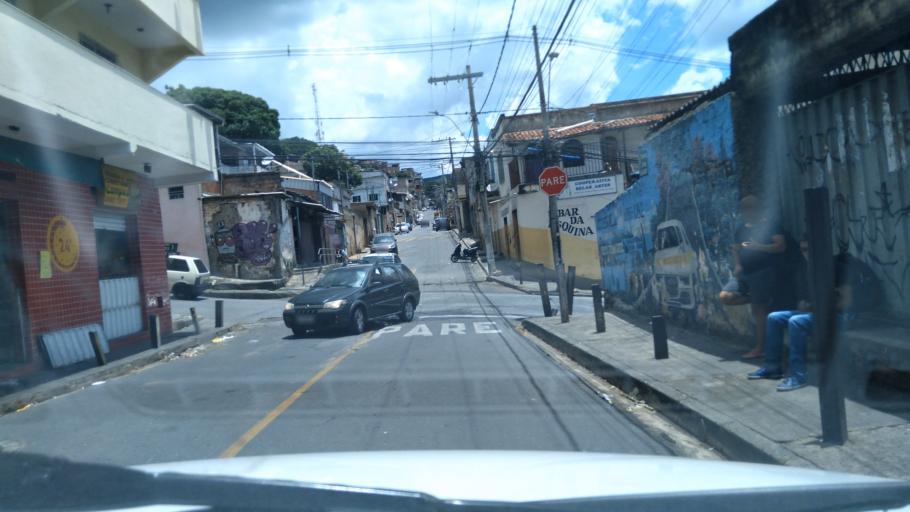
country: BR
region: Minas Gerais
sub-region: Belo Horizonte
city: Belo Horizonte
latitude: -19.9096
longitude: -43.8924
